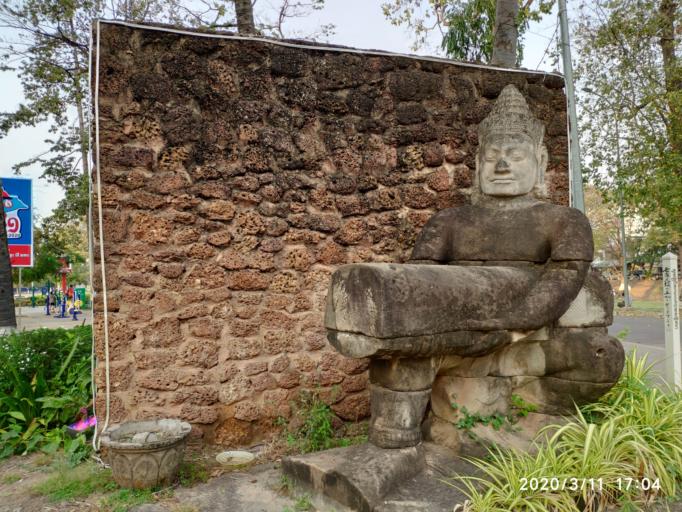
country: KH
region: Siem Reap
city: Siem Reap
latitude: 13.3619
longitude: 103.8601
